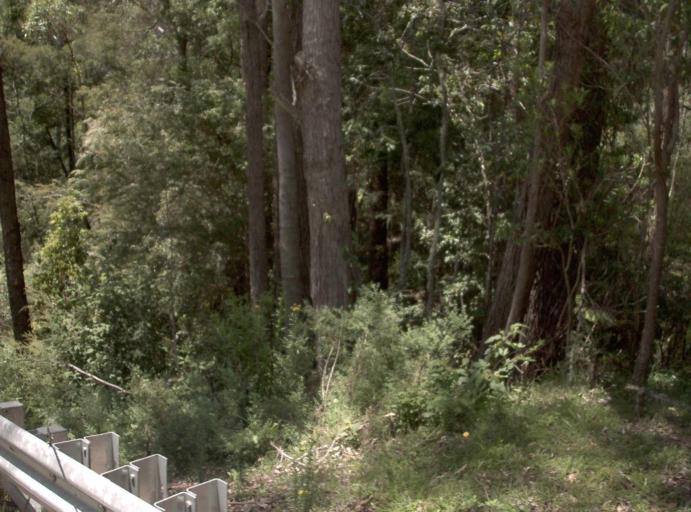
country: AU
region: New South Wales
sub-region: Bombala
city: Bombala
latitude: -37.5349
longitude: 148.9294
